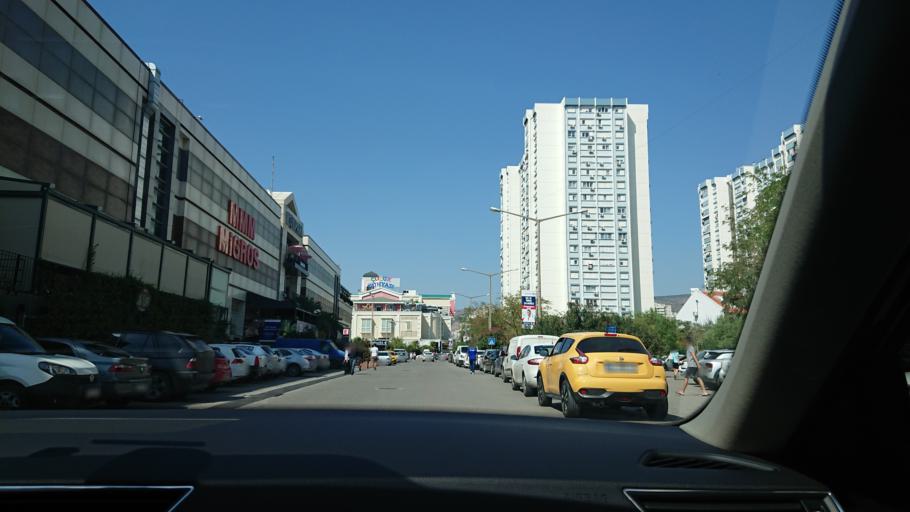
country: TR
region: Izmir
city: Karsiyaka
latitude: 38.4703
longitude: 27.0755
